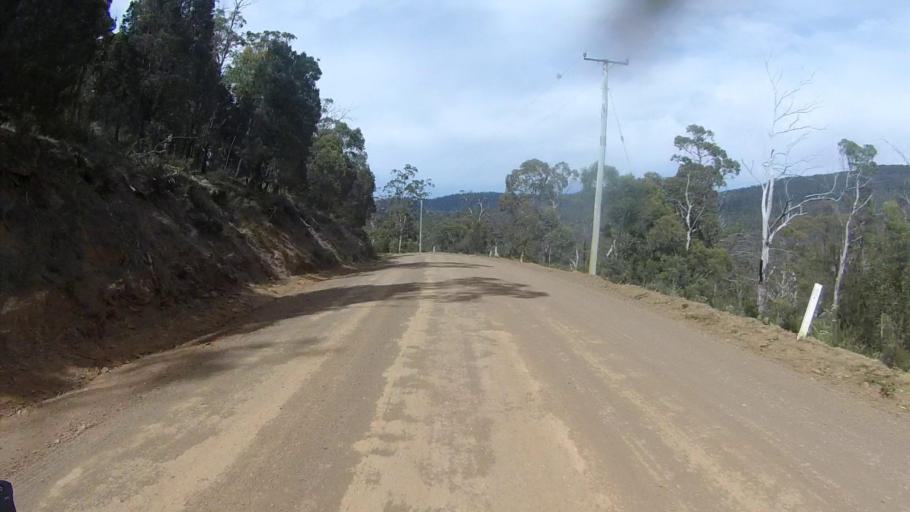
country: AU
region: Tasmania
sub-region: Sorell
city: Sorell
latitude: -42.6690
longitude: 147.8848
